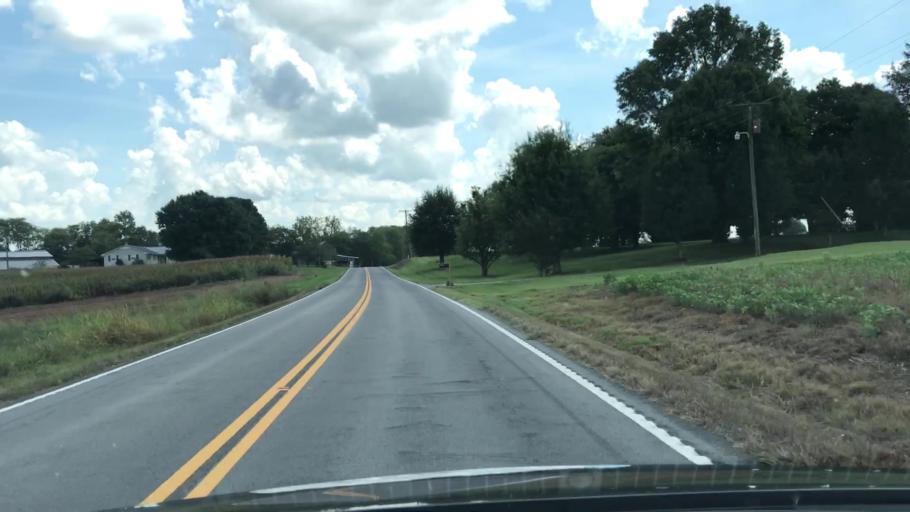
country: US
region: Tennessee
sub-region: Robertson County
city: Springfield
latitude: 36.5761
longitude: -86.8700
